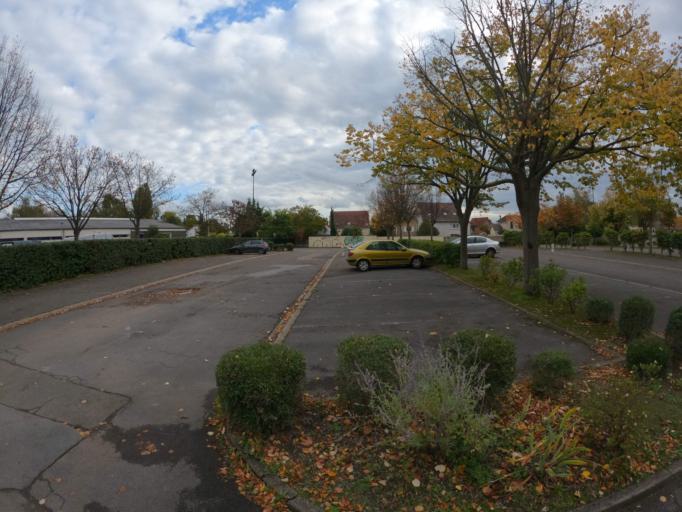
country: FR
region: Ile-de-France
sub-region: Departement de Seine-et-Marne
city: Chelles
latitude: 48.8825
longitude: 2.5796
